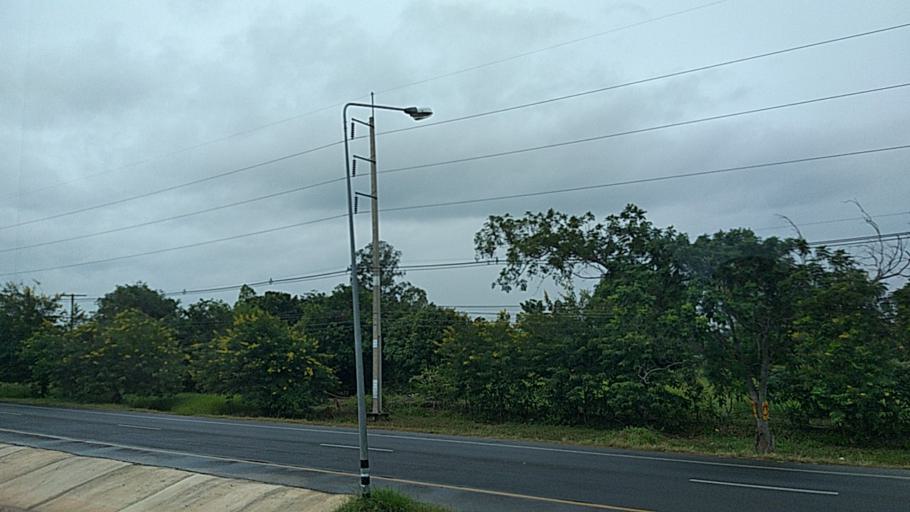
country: TH
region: Maha Sarakham
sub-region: Amphoe Borabue
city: Borabue
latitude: 16.0660
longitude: 103.1441
